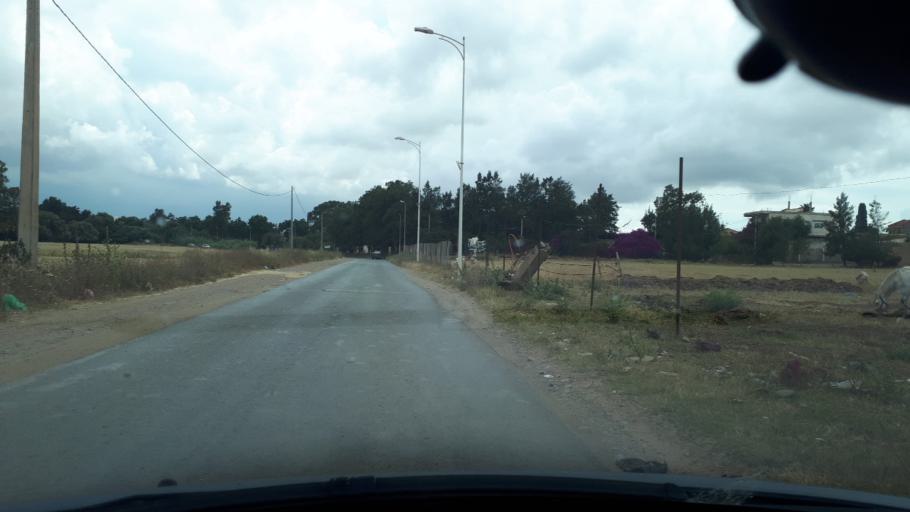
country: DZ
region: Tipaza
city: Cheraga
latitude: 36.7373
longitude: 2.9070
